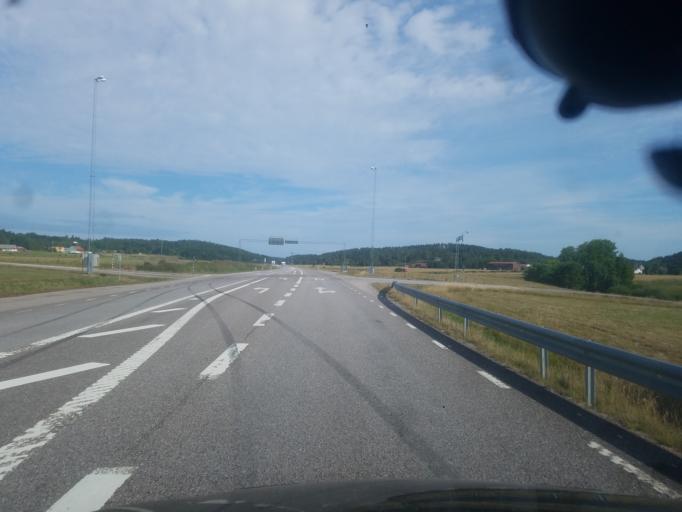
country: SE
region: Vaestra Goetaland
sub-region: Orust
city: Henan
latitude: 58.1635
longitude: 11.7054
